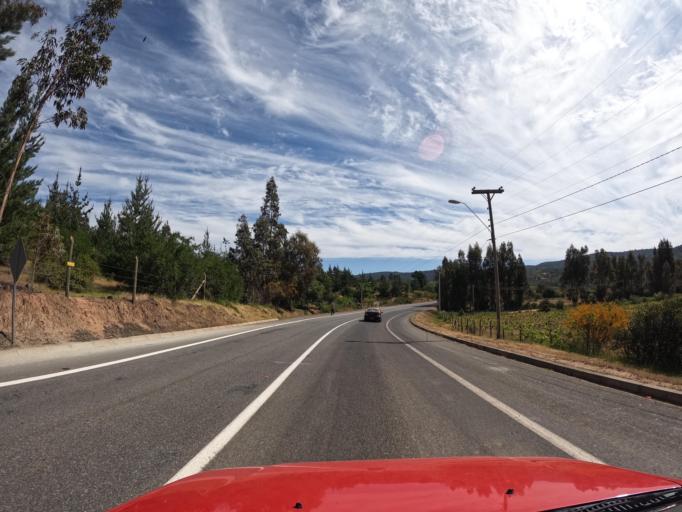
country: CL
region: Maule
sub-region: Provincia de Talca
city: Talca
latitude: -35.1305
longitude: -71.9568
